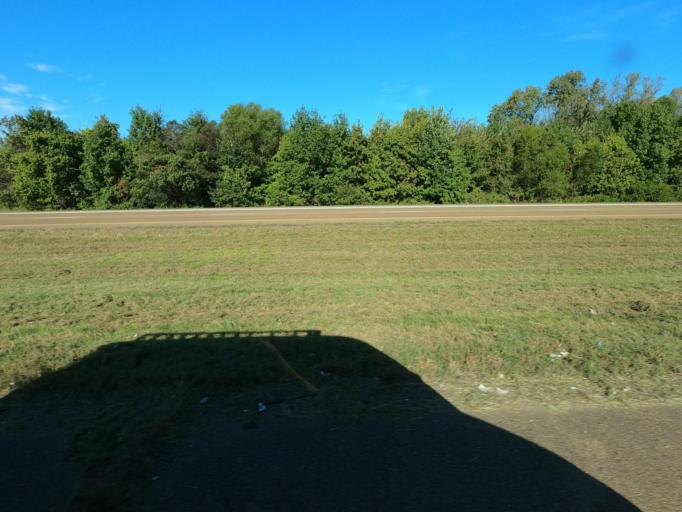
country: US
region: Tennessee
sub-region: Shelby County
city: Millington
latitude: 35.3645
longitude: -89.8891
